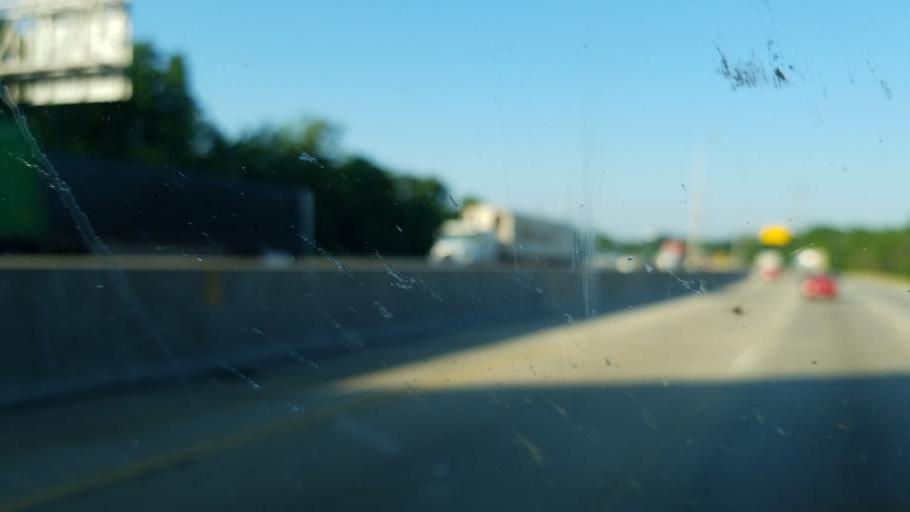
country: US
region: Illinois
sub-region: Will County
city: New Lenox
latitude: 41.5311
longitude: -87.9859
